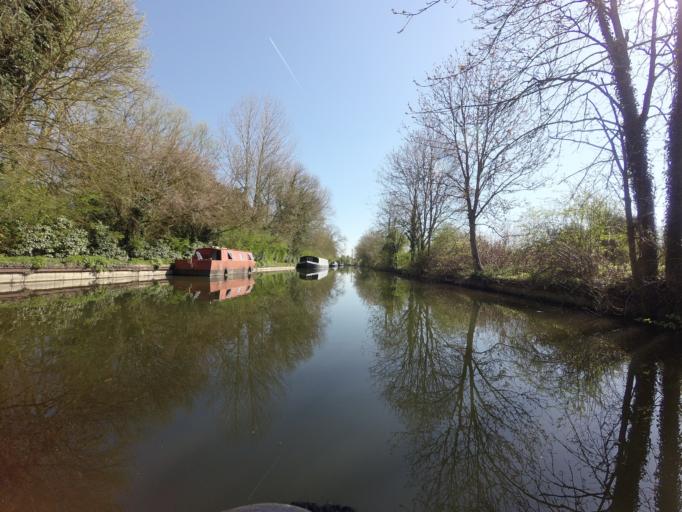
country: GB
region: England
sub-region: Hertfordshire
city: Rickmansworth
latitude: 51.6312
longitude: -0.4791
